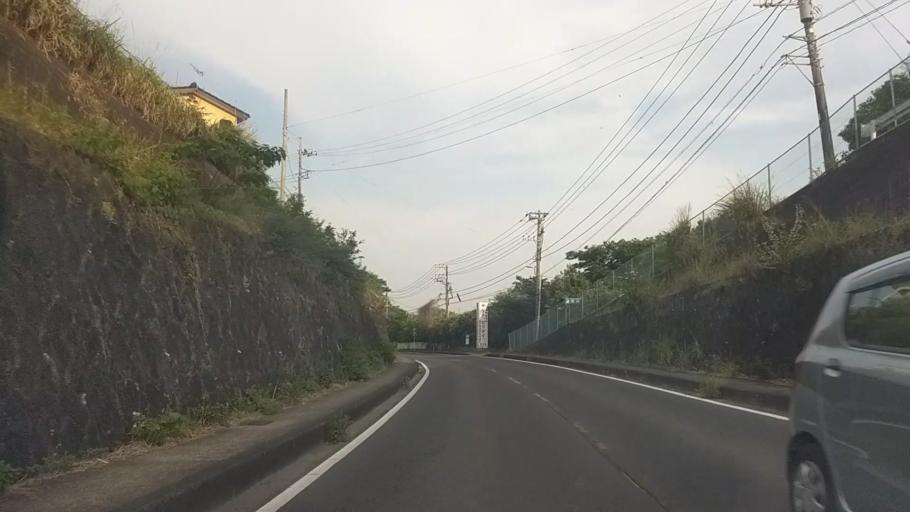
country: JP
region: Kanagawa
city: Odawara
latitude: 35.3116
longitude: 139.1180
